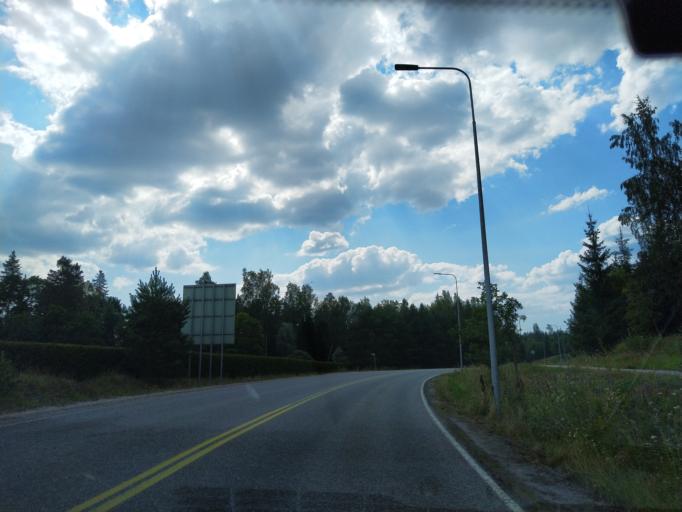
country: FI
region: Uusimaa
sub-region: Helsinki
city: Kirkkonummi
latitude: 60.1169
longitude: 24.4821
